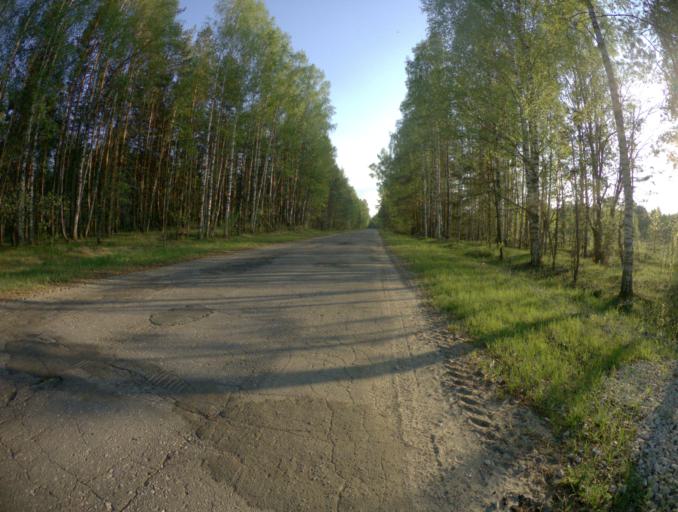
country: RU
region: Vladimir
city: Vyazniki
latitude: 56.3335
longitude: 42.1283
